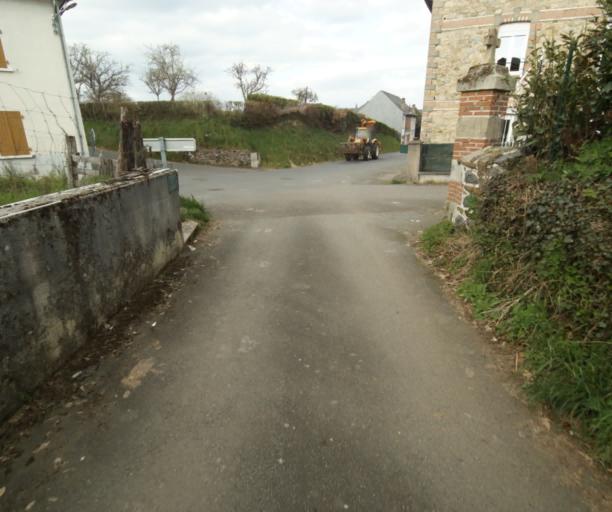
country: FR
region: Limousin
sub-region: Departement de la Correze
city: Saint-Clement
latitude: 45.3516
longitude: 1.6356
